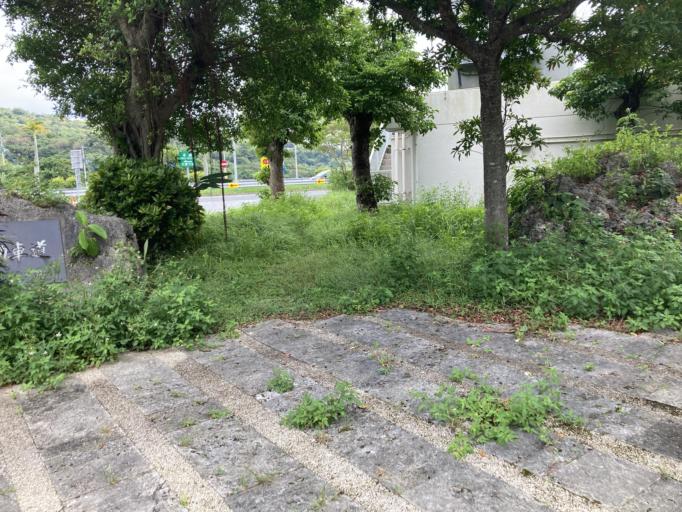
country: JP
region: Okinawa
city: Ginowan
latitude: 26.2766
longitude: 127.7808
